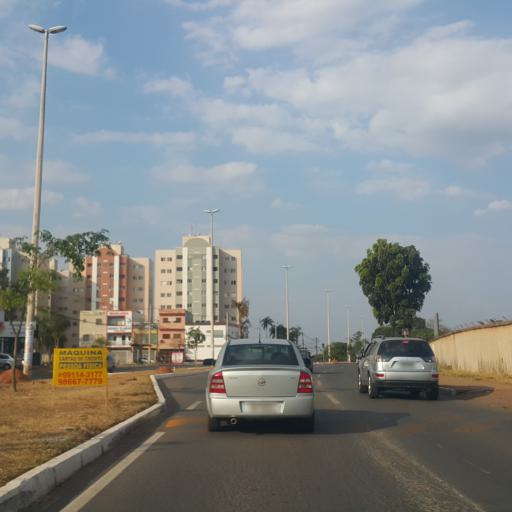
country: BR
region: Federal District
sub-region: Brasilia
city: Brasilia
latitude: -15.8703
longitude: -48.0269
